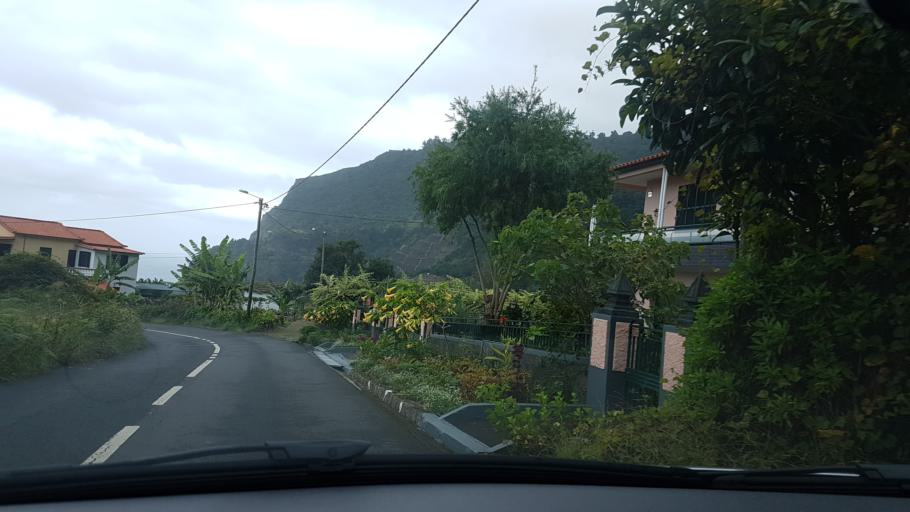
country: PT
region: Madeira
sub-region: Santana
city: Santana
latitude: 32.8236
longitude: -16.9581
